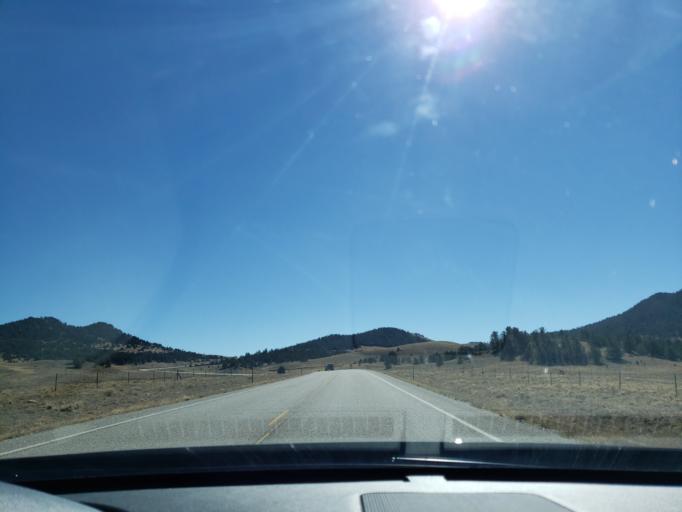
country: US
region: Colorado
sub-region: Chaffee County
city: Salida
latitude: 38.8510
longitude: -105.6512
